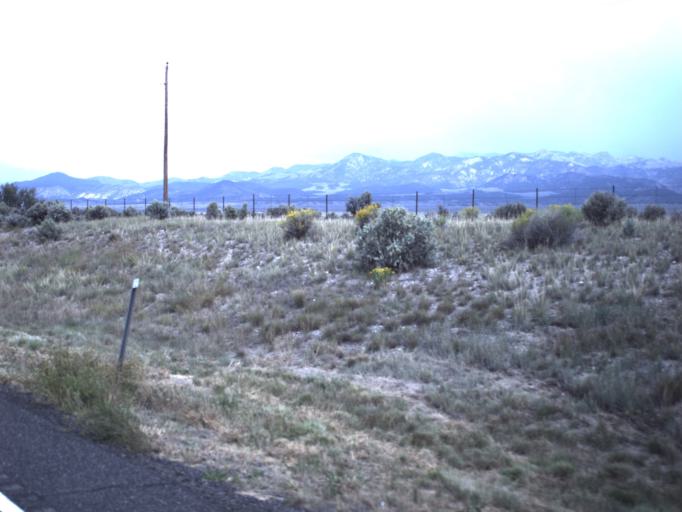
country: US
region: Utah
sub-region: Garfield County
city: Panguitch
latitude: 37.9468
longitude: -112.4208
